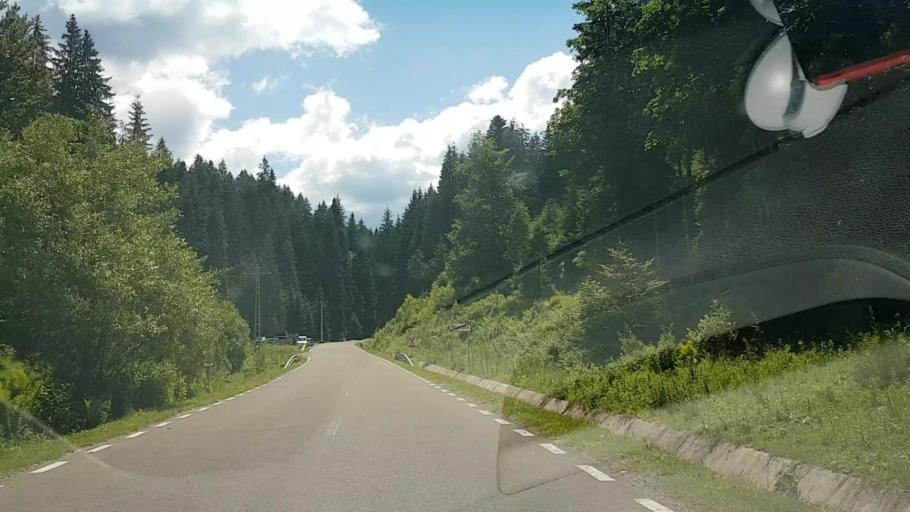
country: RO
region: Suceava
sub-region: Comuna Sadova
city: Sadova
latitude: 47.4793
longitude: 25.4941
